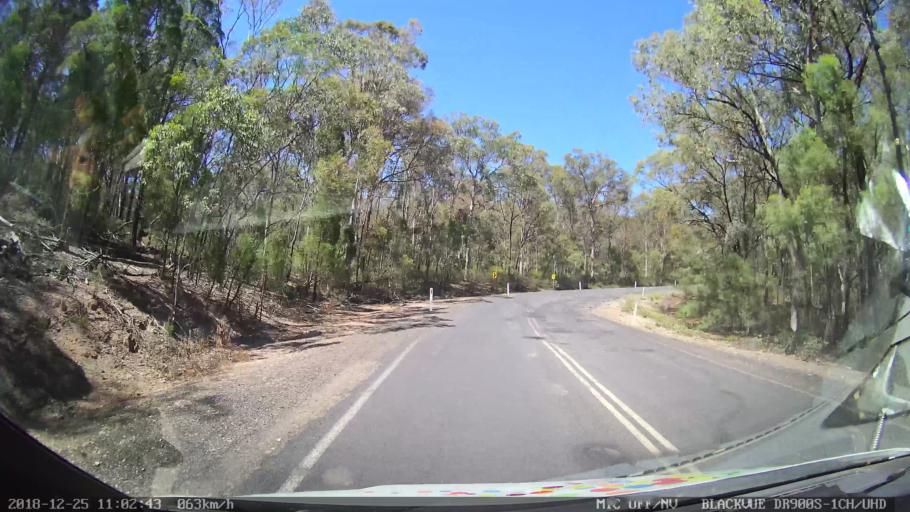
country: AU
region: New South Wales
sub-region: Upper Hunter Shire
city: Merriwa
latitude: -32.4058
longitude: 150.1879
